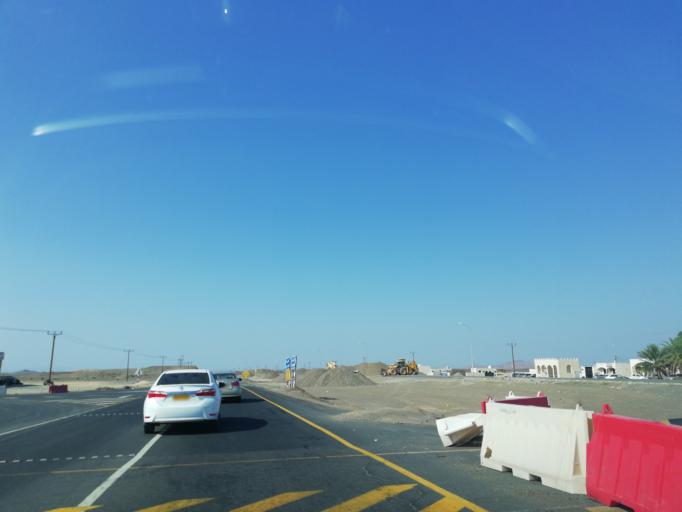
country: OM
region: Ash Sharqiyah
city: Ibra'
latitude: 22.7032
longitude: 58.1411
